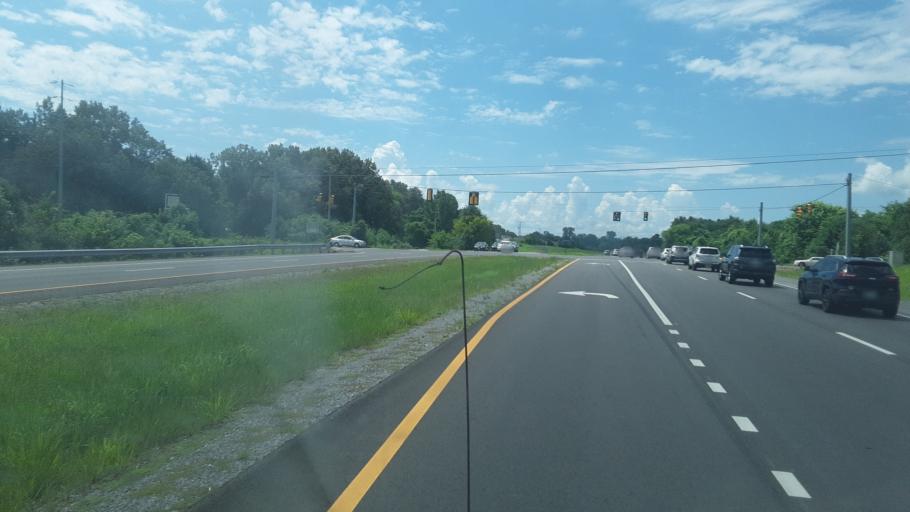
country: US
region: Kentucky
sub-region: Christian County
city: Fort Campbell North
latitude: 36.5768
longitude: -87.4457
